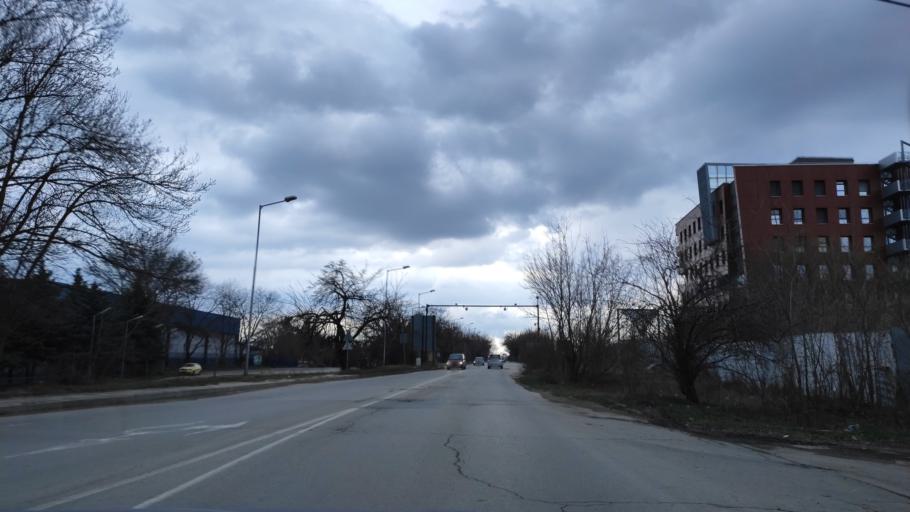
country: BG
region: Varna
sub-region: Obshtina Aksakovo
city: Aksakovo
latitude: 43.2260
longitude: 27.8581
